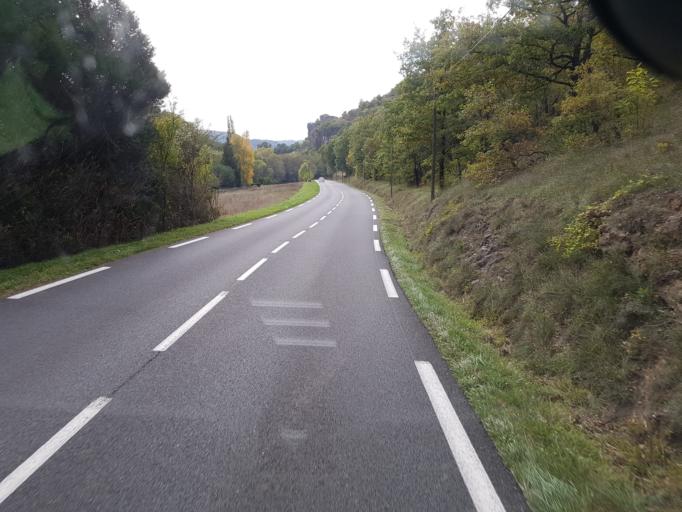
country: FR
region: Midi-Pyrenees
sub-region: Departement de l'Aveyron
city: Saint-Affrique
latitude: 43.9726
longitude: 2.9034
